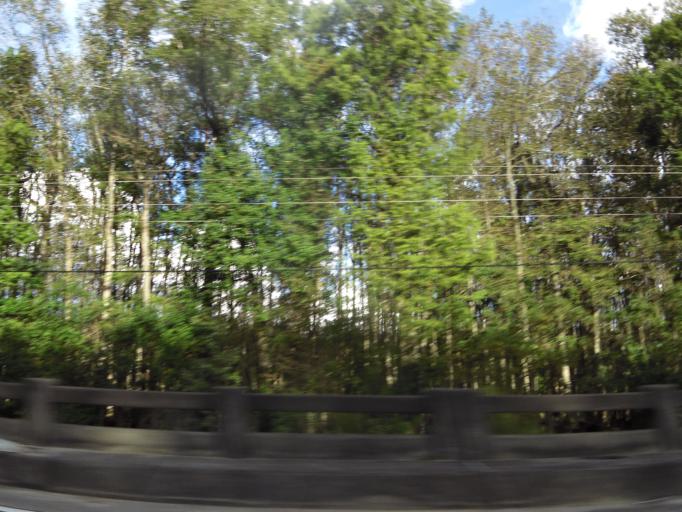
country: US
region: Georgia
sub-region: Liberty County
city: Midway
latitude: 31.8180
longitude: -81.4299
